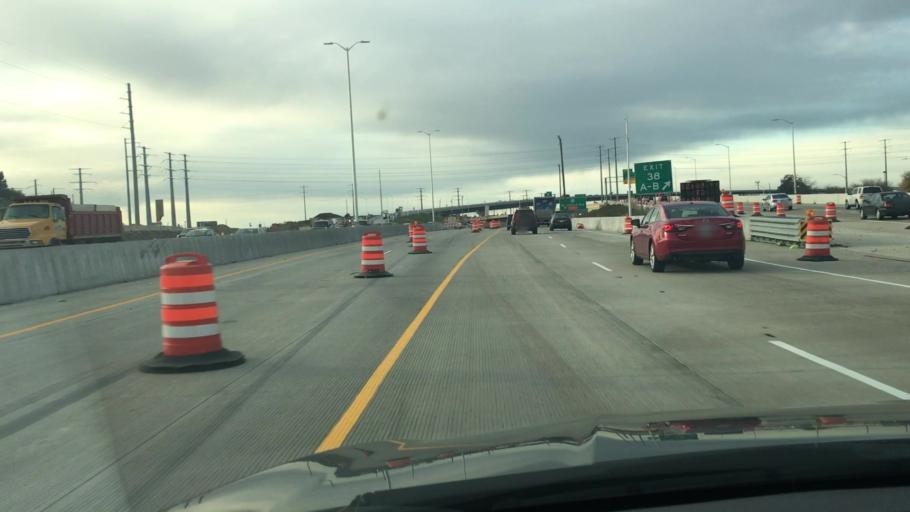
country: US
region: Wisconsin
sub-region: Milwaukee County
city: Wauwatosa
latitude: 43.0336
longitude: -88.0337
